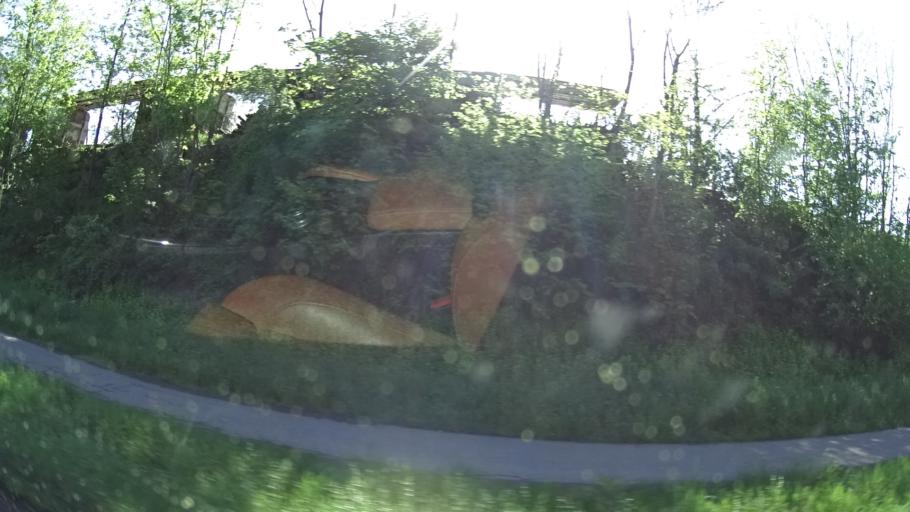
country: DE
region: Baden-Wuerttemberg
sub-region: Karlsruhe Region
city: Rohrdorf
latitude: 48.5624
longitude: 8.6976
